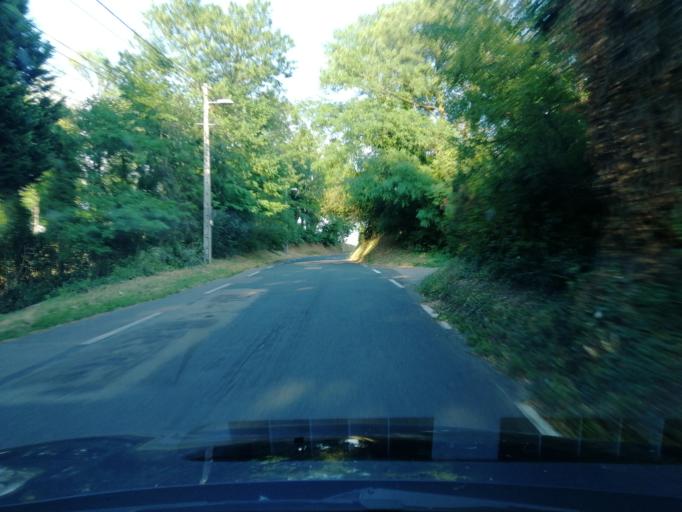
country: FR
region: Rhone-Alpes
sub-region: Departement du Rhone
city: Fontaines-Saint-Martin
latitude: 45.8396
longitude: 4.8596
